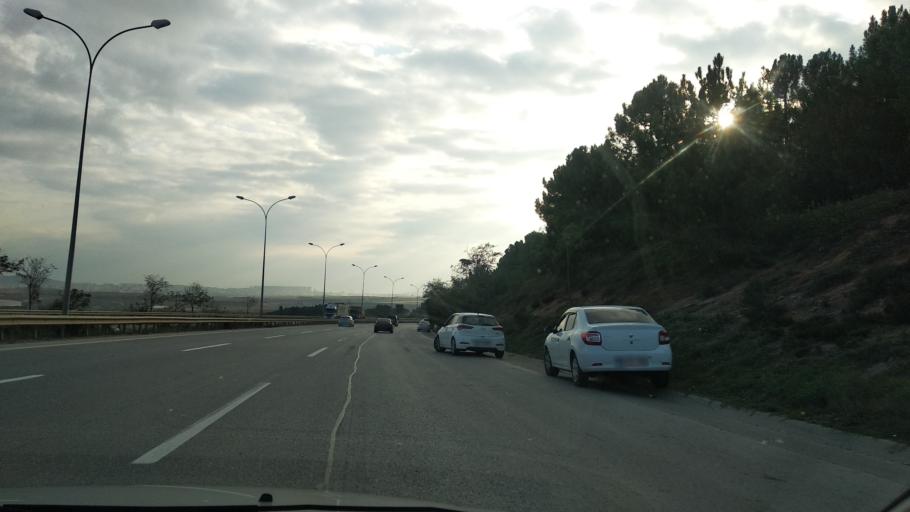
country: TR
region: Istanbul
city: Pendik
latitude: 40.9195
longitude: 29.3386
